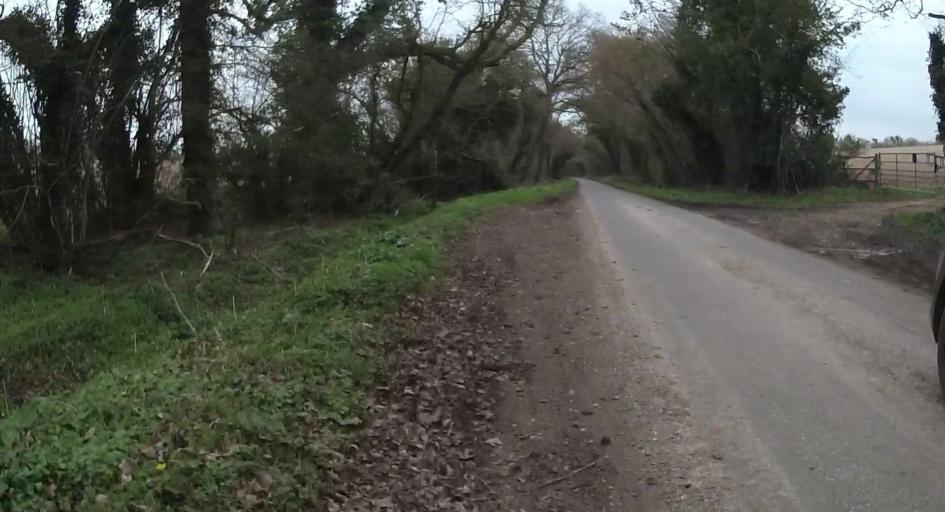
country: GB
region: England
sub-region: Hampshire
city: Four Marks
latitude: 51.1051
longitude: -1.1158
